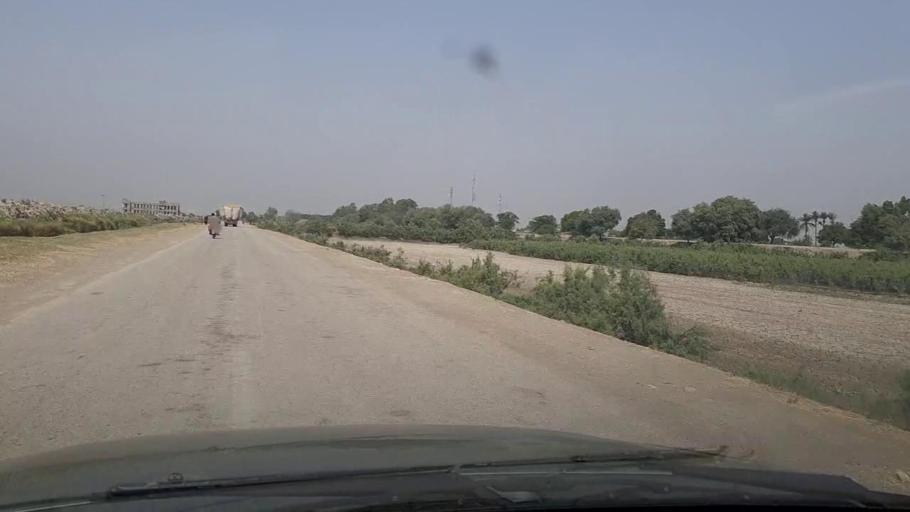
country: PK
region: Sindh
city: Thul
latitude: 28.3230
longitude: 68.7442
